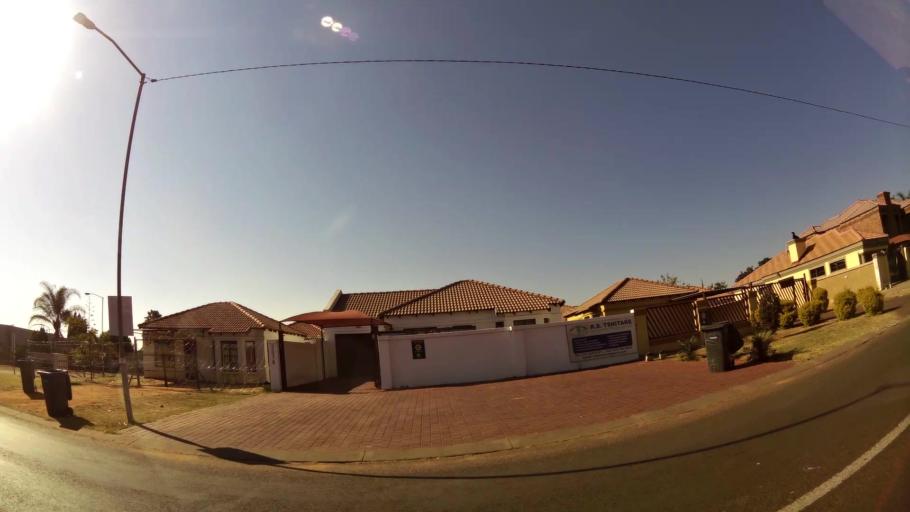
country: ZA
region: North-West
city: Ga-Rankuwa
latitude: -25.6681
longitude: 28.0921
